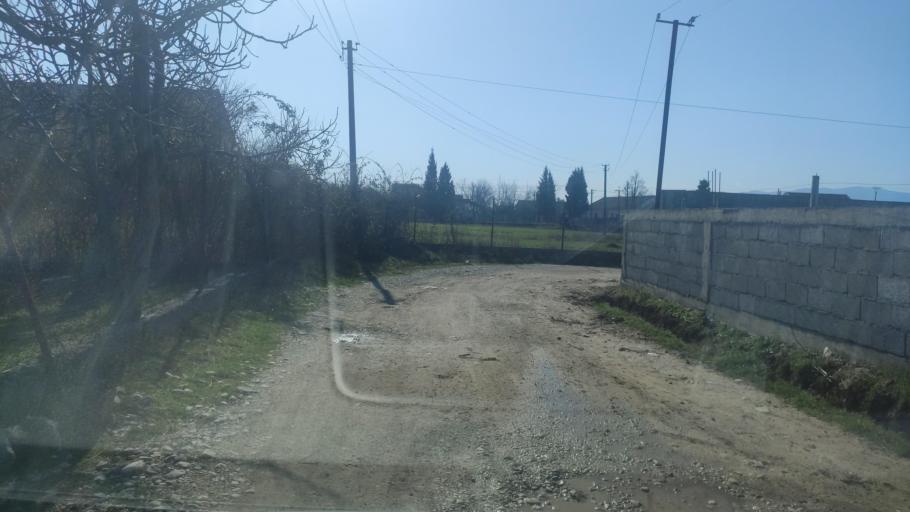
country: AL
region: Shkoder
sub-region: Rrethi i Malesia e Madhe
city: Grude-Fushe
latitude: 42.1625
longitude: 19.4579
